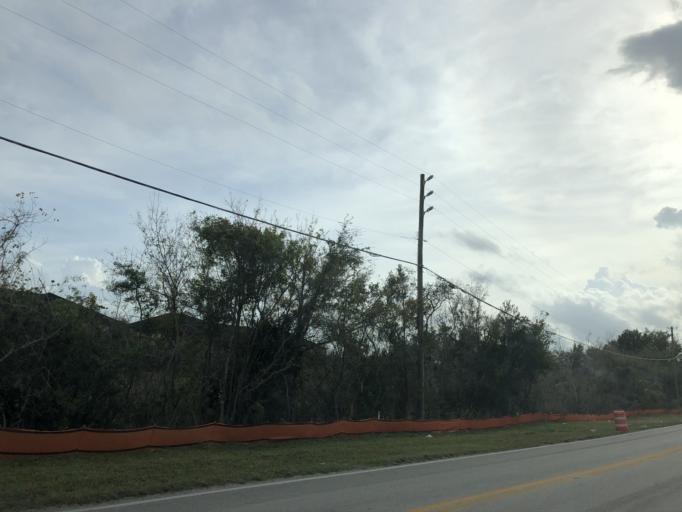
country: US
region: Florida
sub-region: Osceola County
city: Buenaventura Lakes
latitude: 28.2823
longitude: -81.3547
